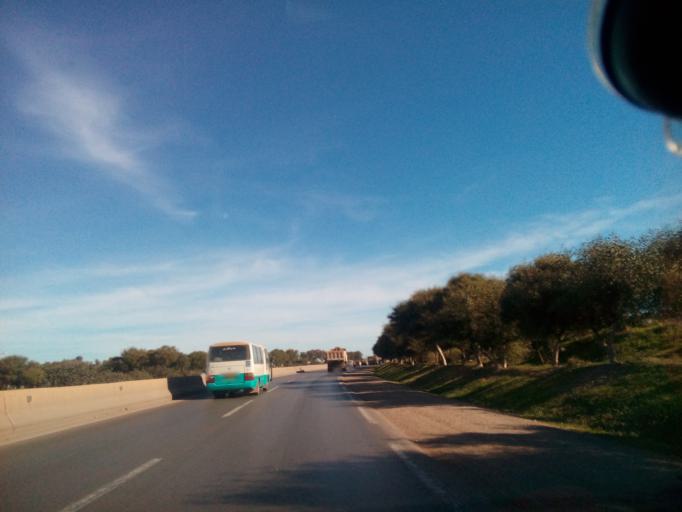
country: DZ
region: Oran
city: Ain el Bya
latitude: 35.7880
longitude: -0.4095
